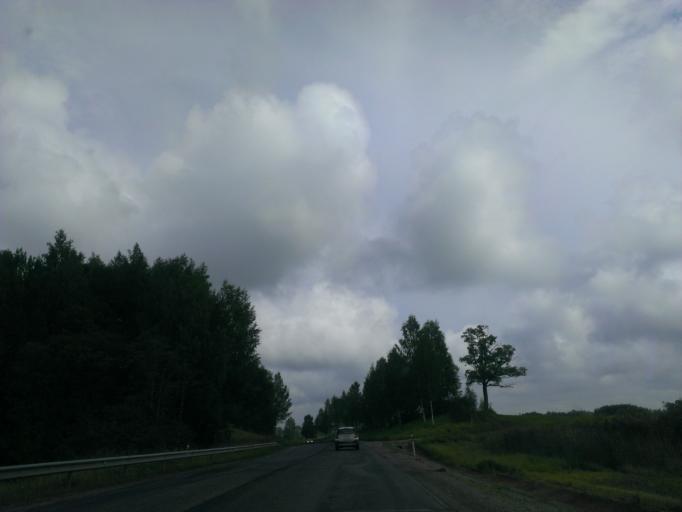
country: LV
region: Ligatne
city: Ligatne
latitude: 57.2040
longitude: 25.1404
